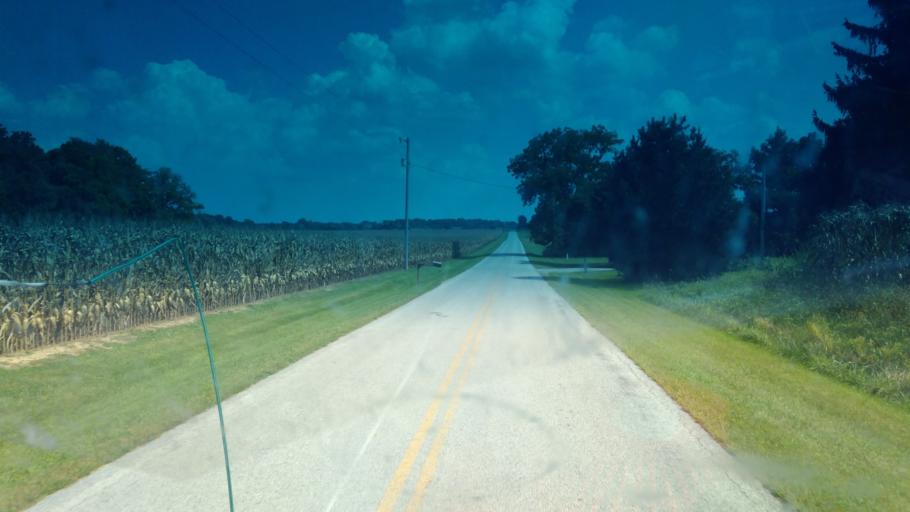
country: US
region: Ohio
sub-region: Hardin County
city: Ada
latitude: 40.7186
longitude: -83.8005
